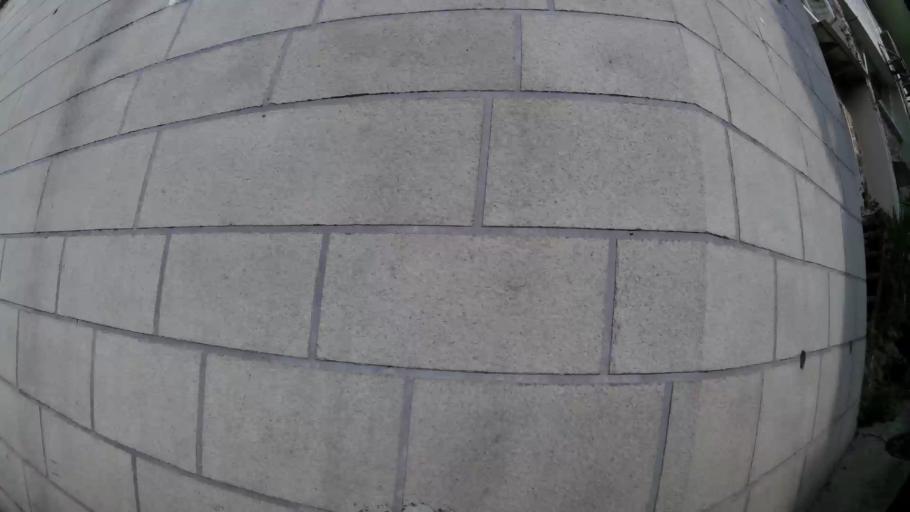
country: HK
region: Wanchai
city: Wan Chai
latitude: 22.2681
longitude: 114.1806
